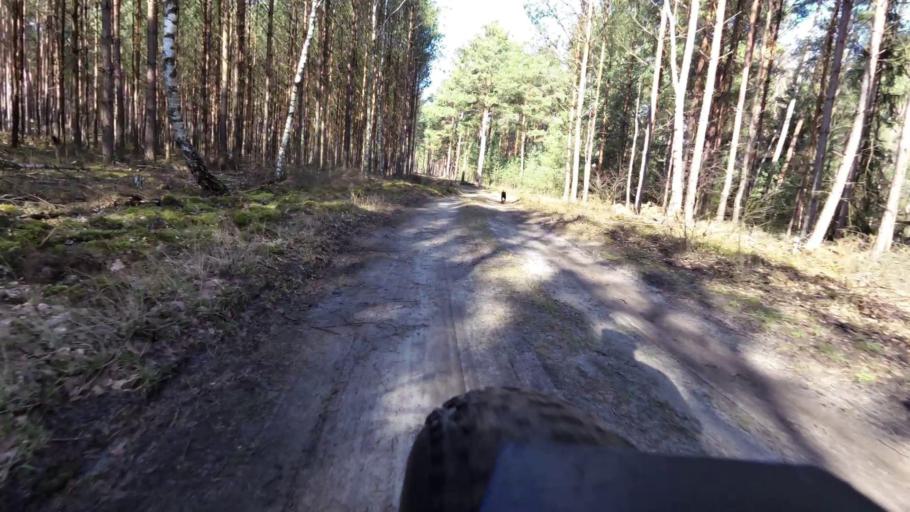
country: PL
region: Lubusz
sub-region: Powiat sulecinski
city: Torzym
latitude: 52.2193
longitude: 14.9915
